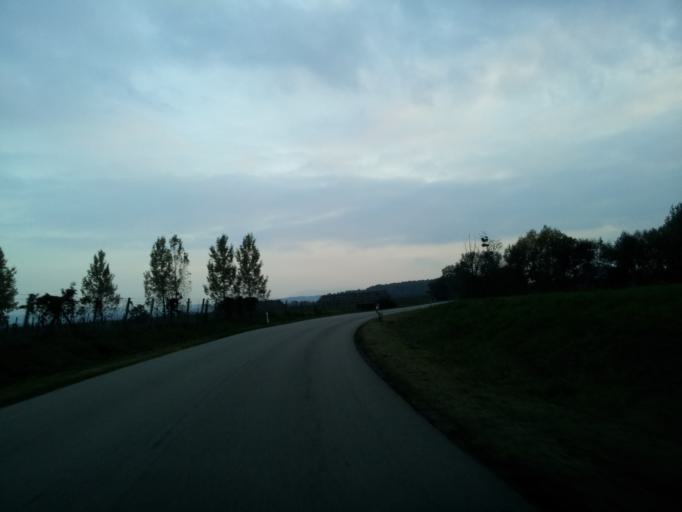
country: HU
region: Gyor-Moson-Sopron
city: Bakonyszentlaszlo
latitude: 47.4152
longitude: 17.8053
